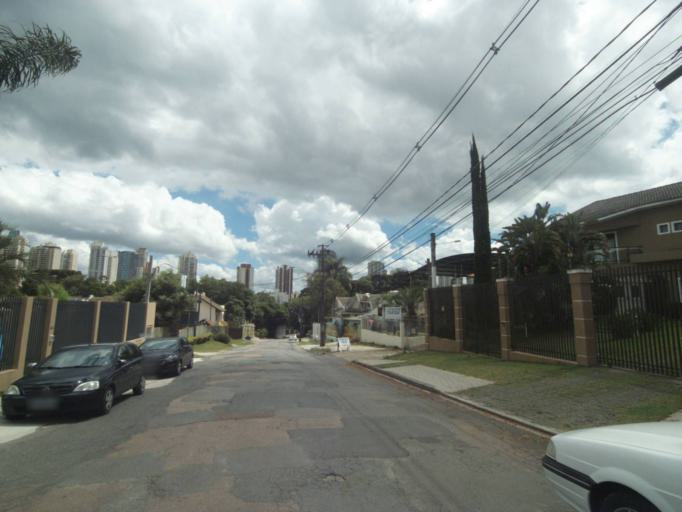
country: BR
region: Parana
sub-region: Curitiba
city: Curitiba
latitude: -25.4332
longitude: -49.3390
